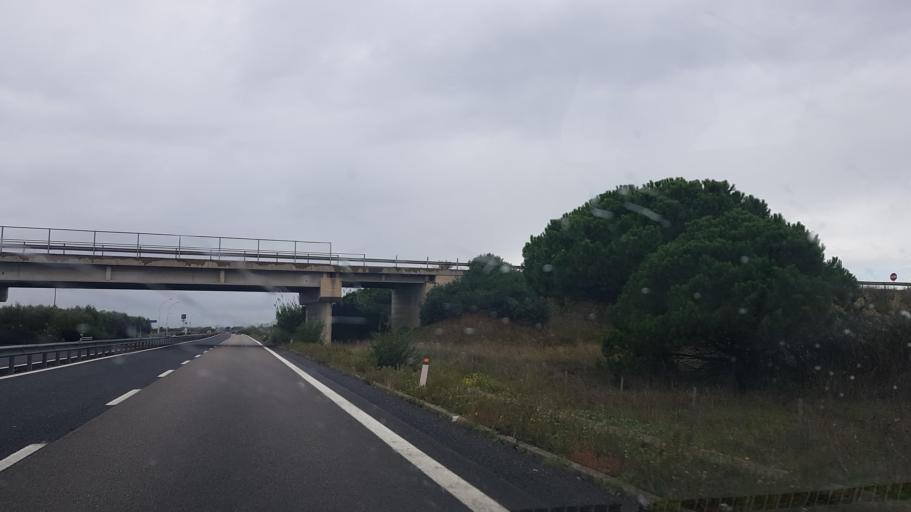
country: IT
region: Apulia
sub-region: Provincia di Taranto
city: Massafra
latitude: 40.5307
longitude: 17.0852
